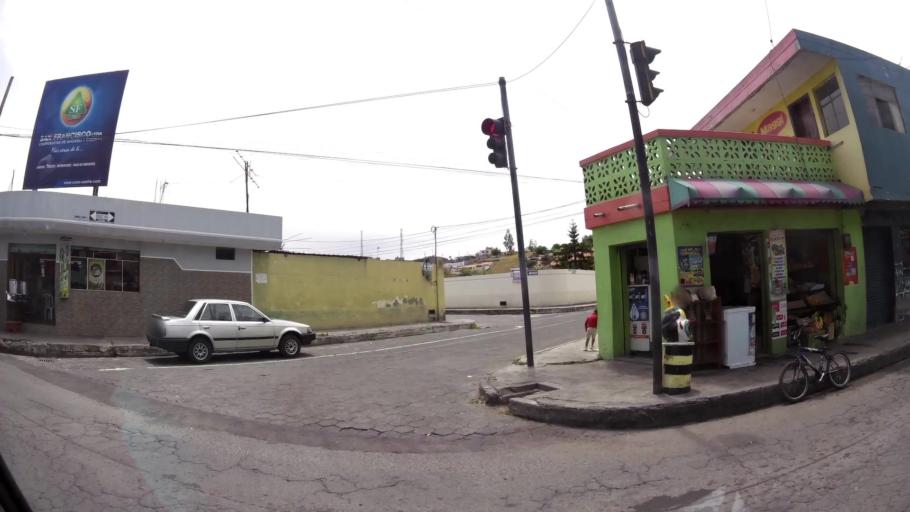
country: EC
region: Cotopaxi
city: San Miguel de Salcedo
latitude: -1.0471
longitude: -78.5924
